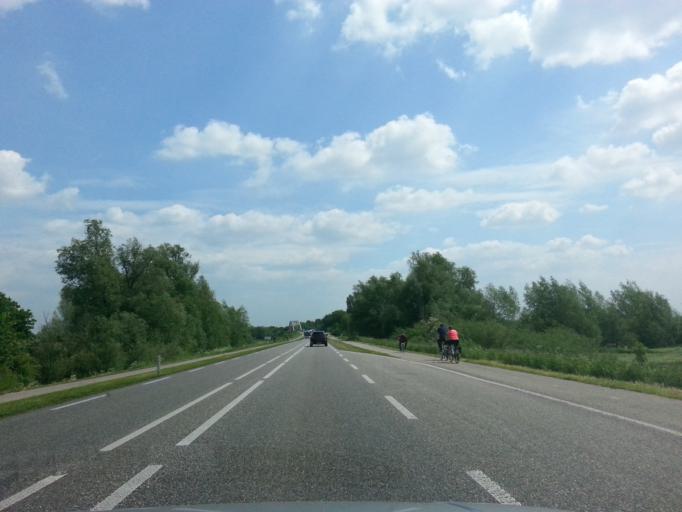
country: NL
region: Gelderland
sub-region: Gemeente Doesburg
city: Doesburg
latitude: 52.0228
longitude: 6.1212
